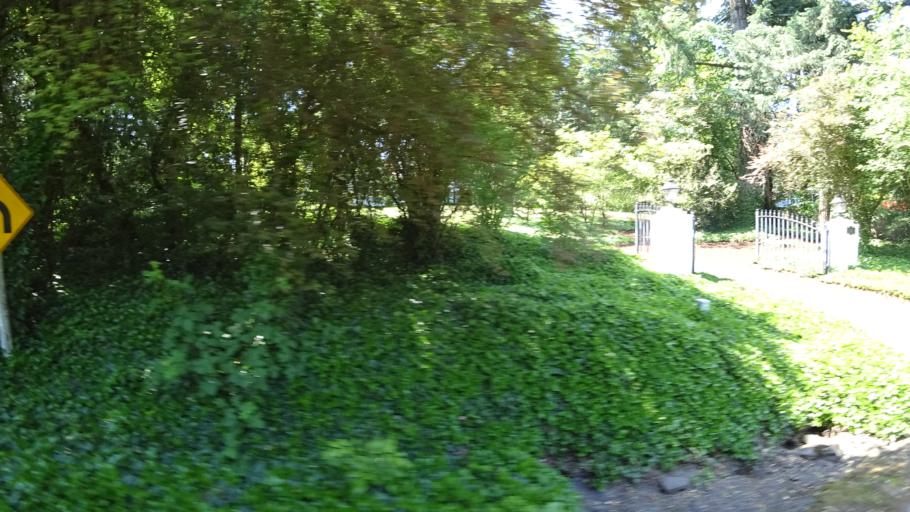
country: US
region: Oregon
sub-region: Clackamas County
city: Lake Oswego
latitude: 45.4295
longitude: -122.6980
